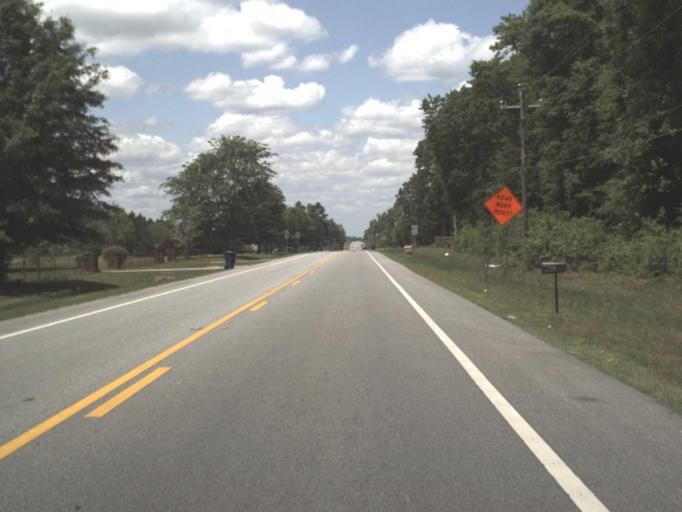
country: US
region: Florida
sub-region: Escambia County
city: Molino
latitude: 30.7258
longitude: -87.3427
